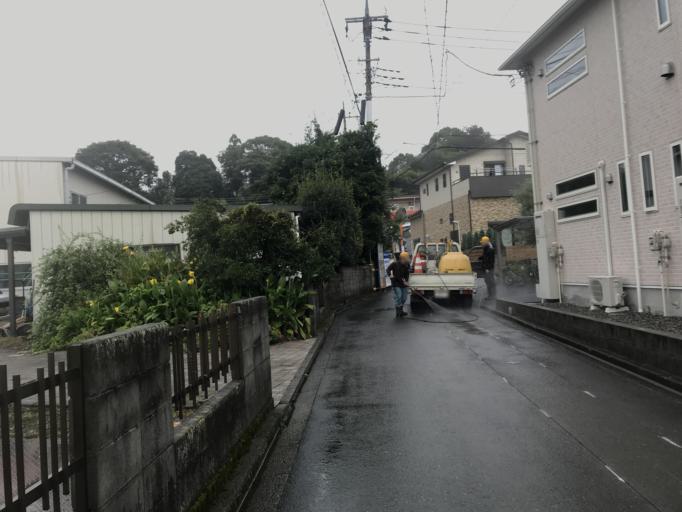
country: JP
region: Kanagawa
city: Zama
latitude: 35.5483
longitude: 139.3266
